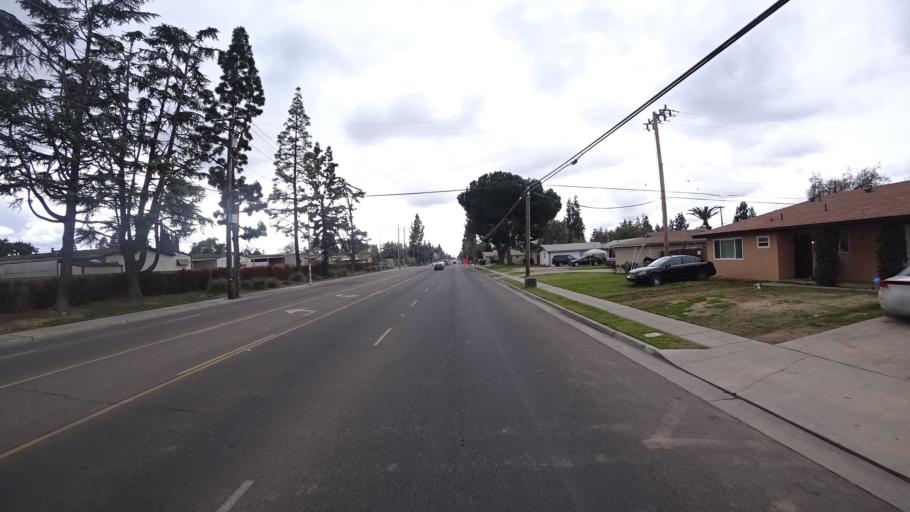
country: US
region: California
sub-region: Fresno County
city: Fresno
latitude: 36.7976
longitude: -119.8444
